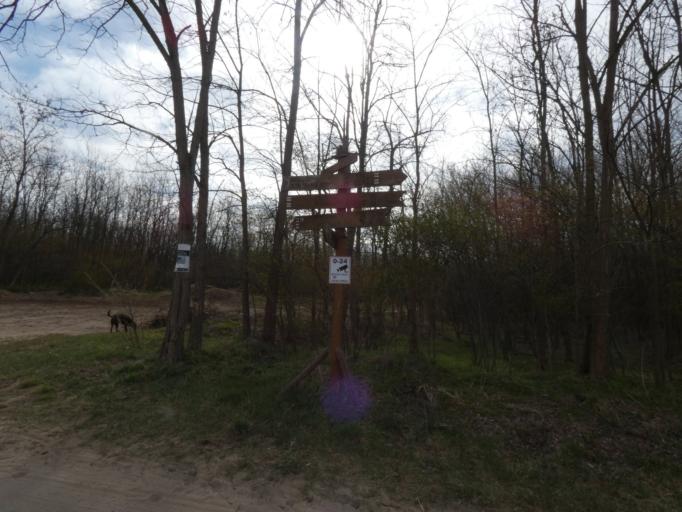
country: HU
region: Pest
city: Kakucs
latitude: 47.2724
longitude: 19.3569
